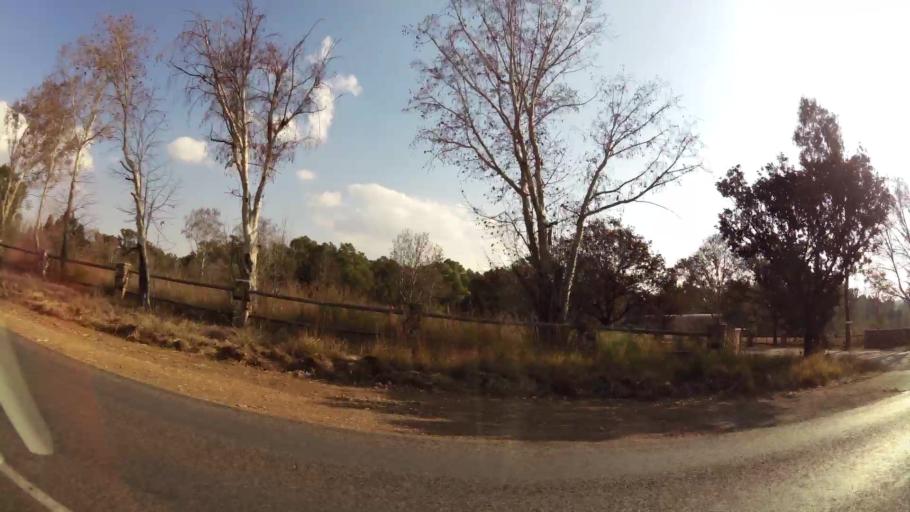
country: ZA
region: Gauteng
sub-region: Ekurhuleni Metropolitan Municipality
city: Tembisa
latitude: -25.9275
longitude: 28.2303
